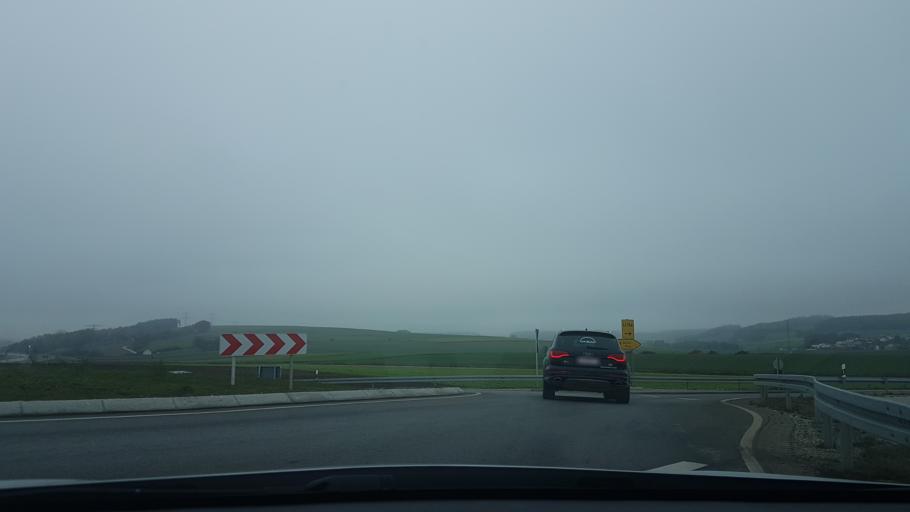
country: DE
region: Bavaria
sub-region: Lower Bavaria
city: Essenbach
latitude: 48.6168
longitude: 12.2319
